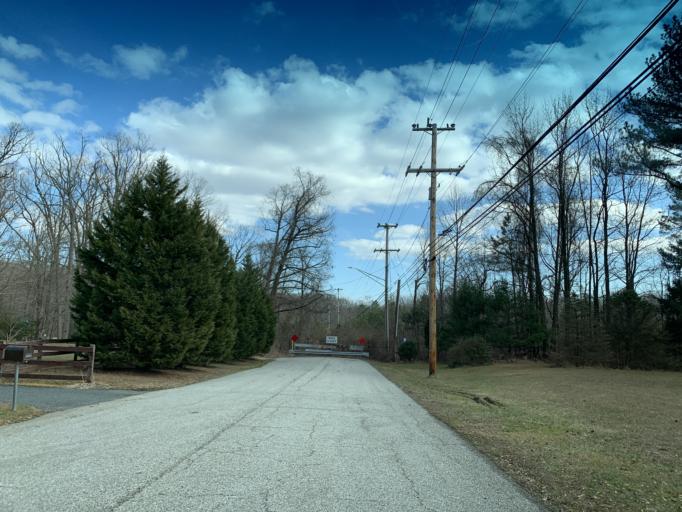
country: US
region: Maryland
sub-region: Harford County
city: Riverside
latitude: 39.4893
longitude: -76.2429
